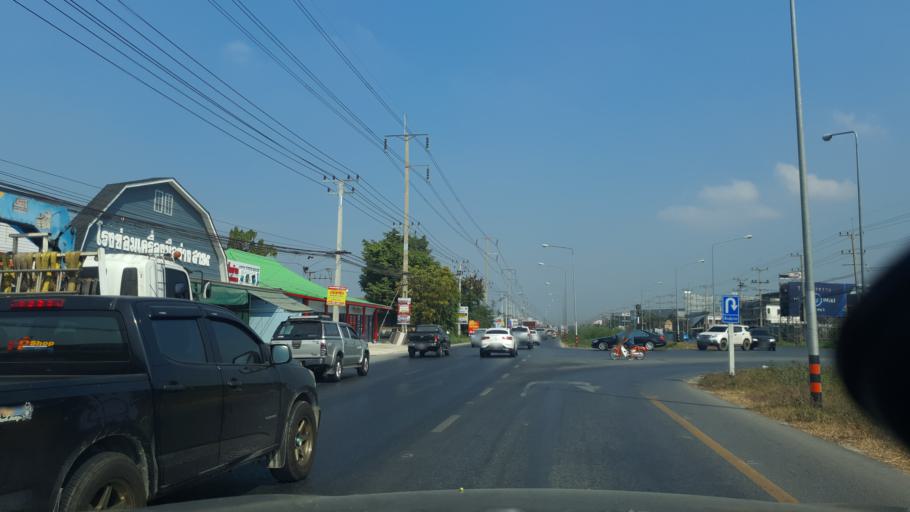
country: TH
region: Nakhon Pathom
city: Salaya
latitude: 13.7774
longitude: 100.3021
